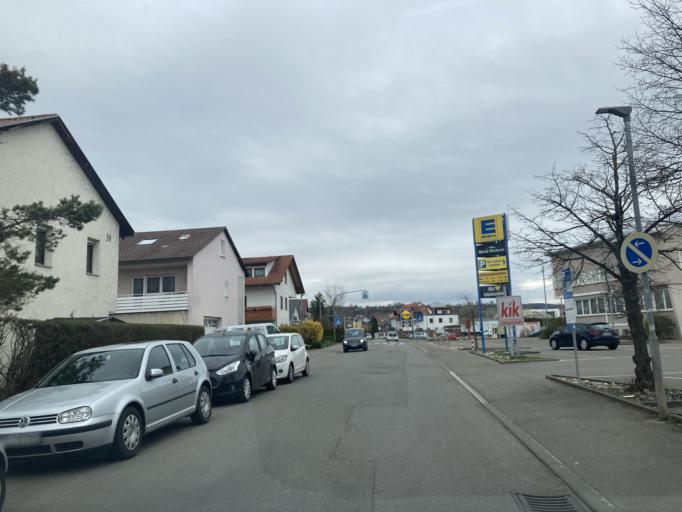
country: DE
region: Baden-Wuerttemberg
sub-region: Tuebingen Region
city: Rottenburg
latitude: 48.4792
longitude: 8.9454
